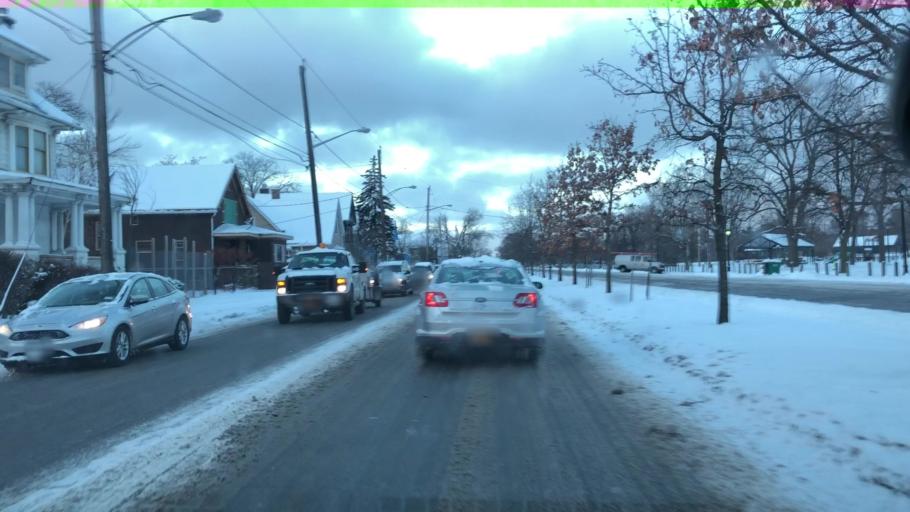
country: US
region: New York
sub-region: Erie County
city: Buffalo
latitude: 42.9037
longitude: -78.8397
